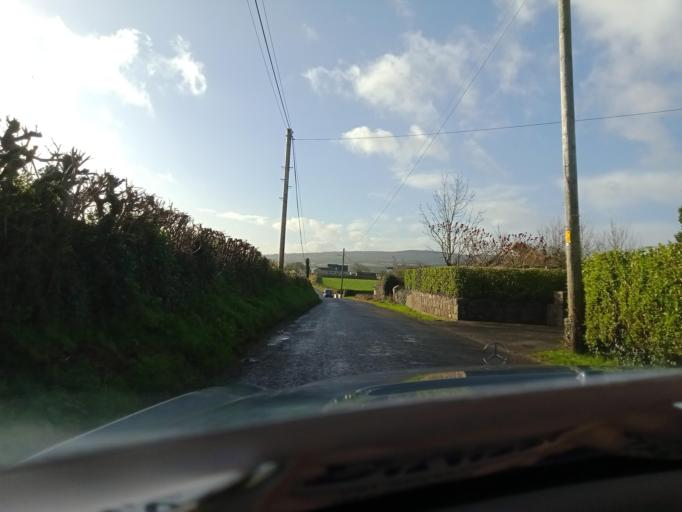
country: IE
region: Leinster
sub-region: Kilkenny
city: Mooncoin
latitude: 52.3278
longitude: -7.2838
